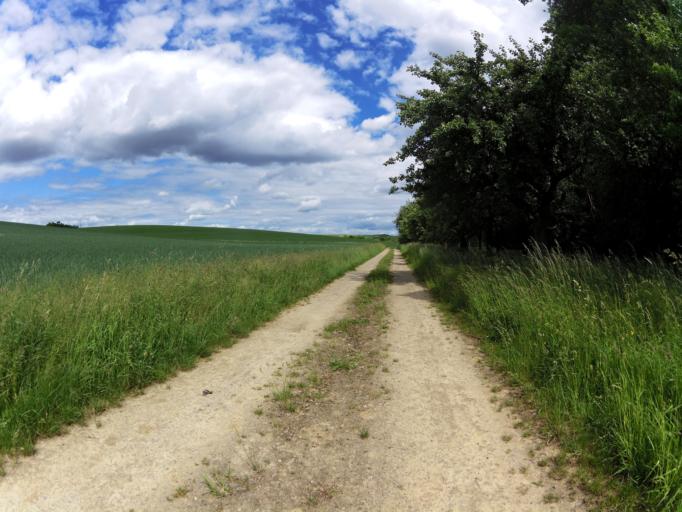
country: DE
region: Bavaria
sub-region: Regierungsbezirk Unterfranken
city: Gaukonigshofen
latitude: 49.6677
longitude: 9.9938
